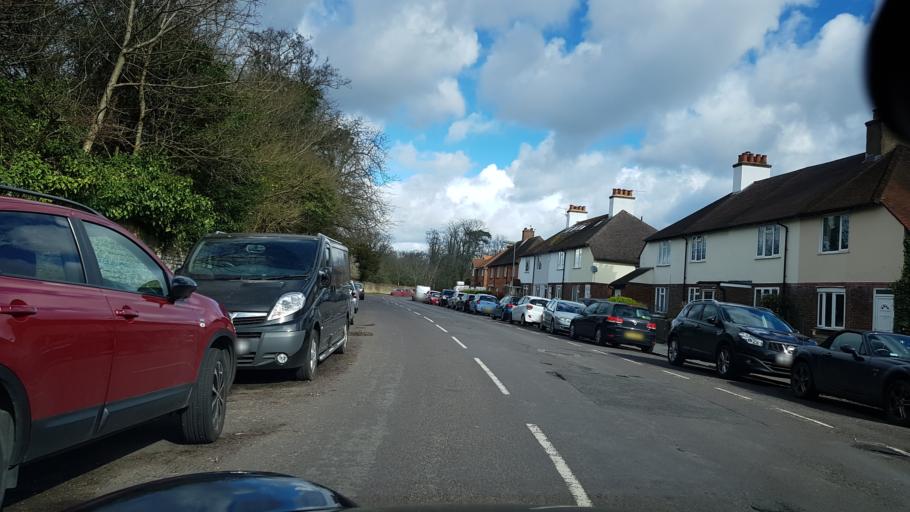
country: GB
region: England
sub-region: Surrey
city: Guildford
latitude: 51.2551
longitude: -0.5733
